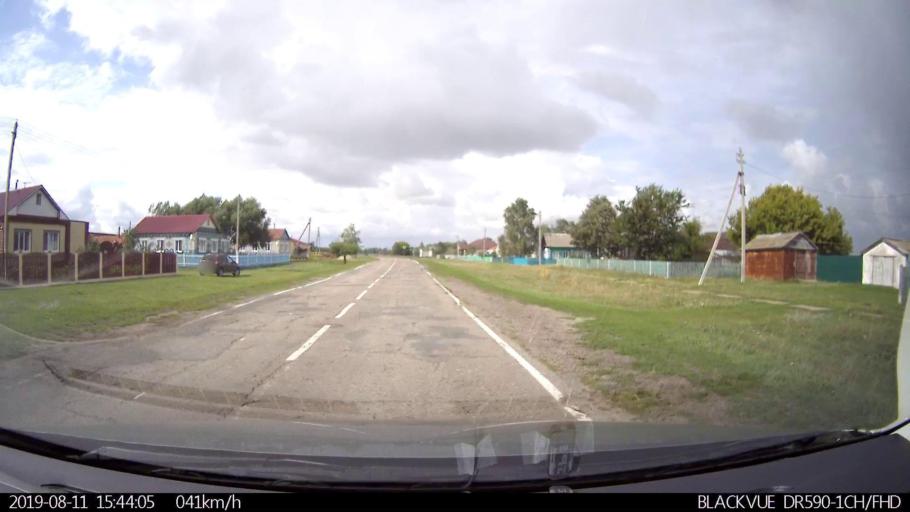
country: RU
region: Ulyanovsk
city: Ignatovka
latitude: 53.8798
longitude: 47.6579
